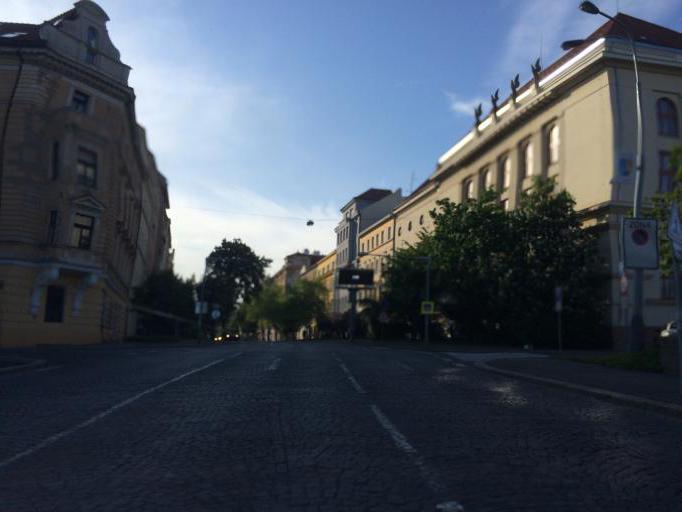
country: CZ
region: Praha
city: Prague
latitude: 50.1022
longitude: 14.4162
